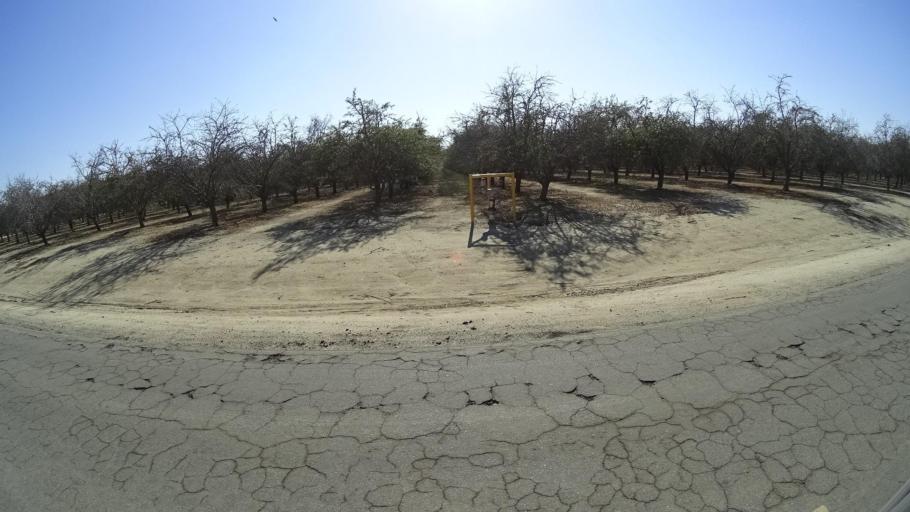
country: US
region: California
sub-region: Kern County
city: McFarland
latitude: 35.7035
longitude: -119.1567
